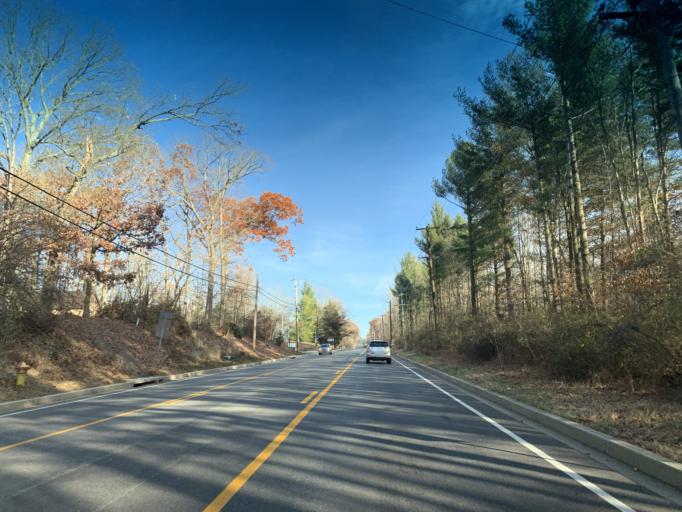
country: US
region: Maryland
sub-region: Cecil County
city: North East
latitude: 39.6021
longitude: -75.9286
